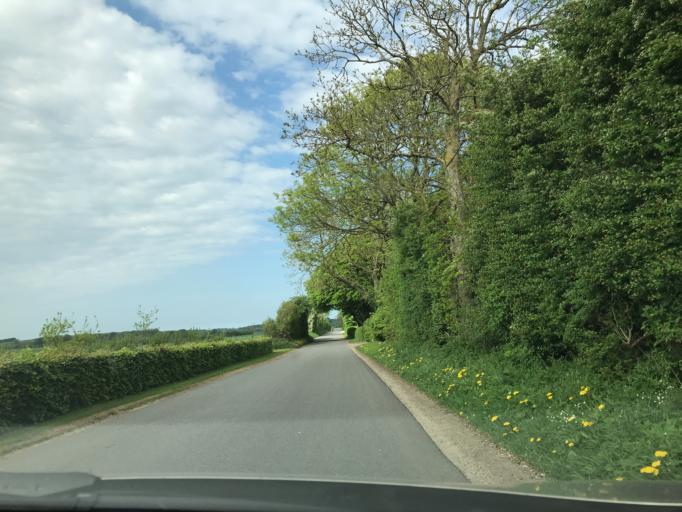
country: DK
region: South Denmark
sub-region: Middelfart Kommune
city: Norre Aby
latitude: 55.3846
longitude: 9.8512
